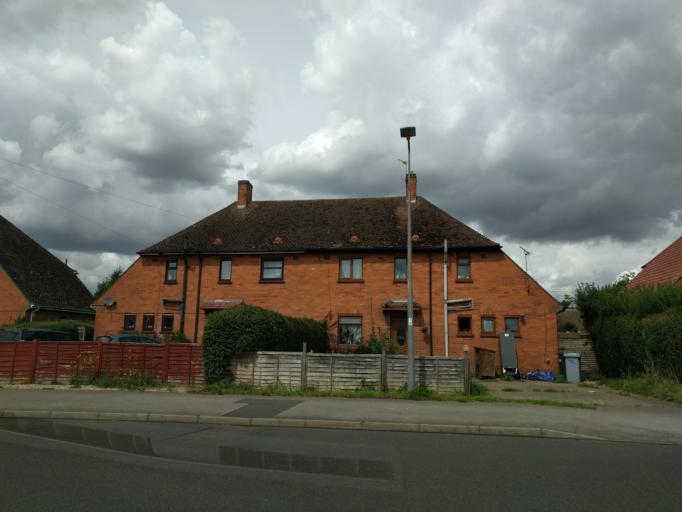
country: GB
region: England
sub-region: Nottinghamshire
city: Farndon
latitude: 53.0622
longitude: -0.8464
